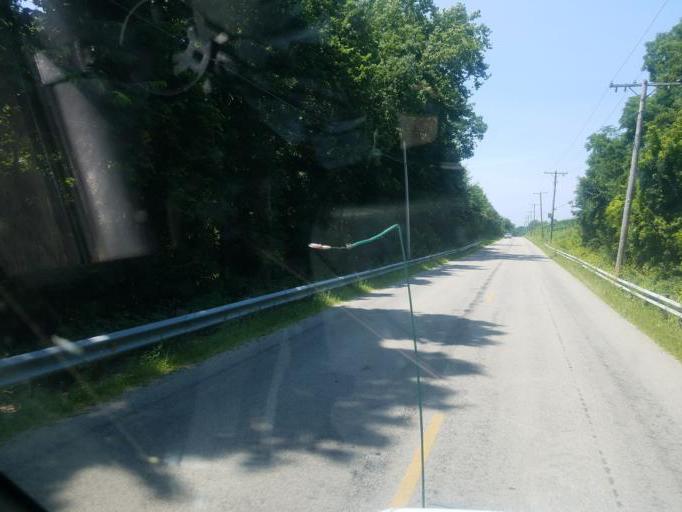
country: US
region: Ohio
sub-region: Shelby County
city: Sidney
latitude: 40.3030
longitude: -84.1283
